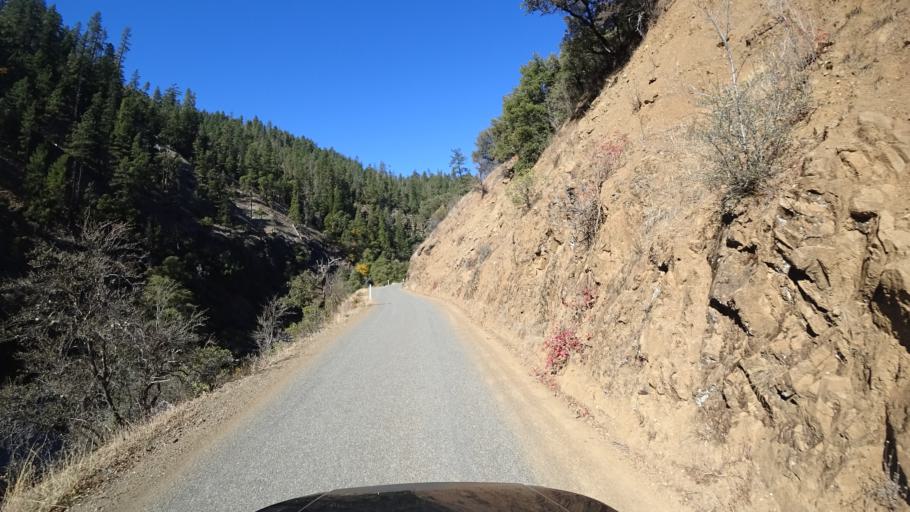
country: US
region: California
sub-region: Humboldt County
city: Willow Creek
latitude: 41.2043
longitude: -123.2255
